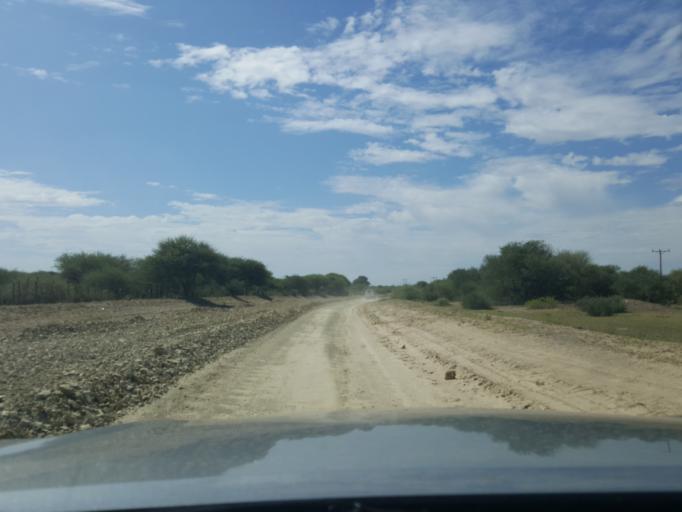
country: BW
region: Kweneng
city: Letlhakeng
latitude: -23.9795
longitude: 24.9666
